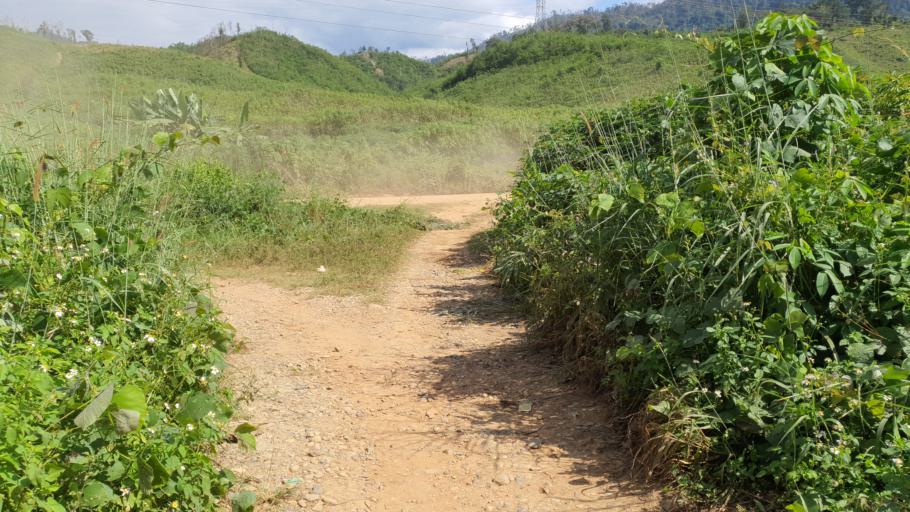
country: LA
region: Bolikhamxai
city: Bolikhan
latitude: 18.9099
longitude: 103.7433
